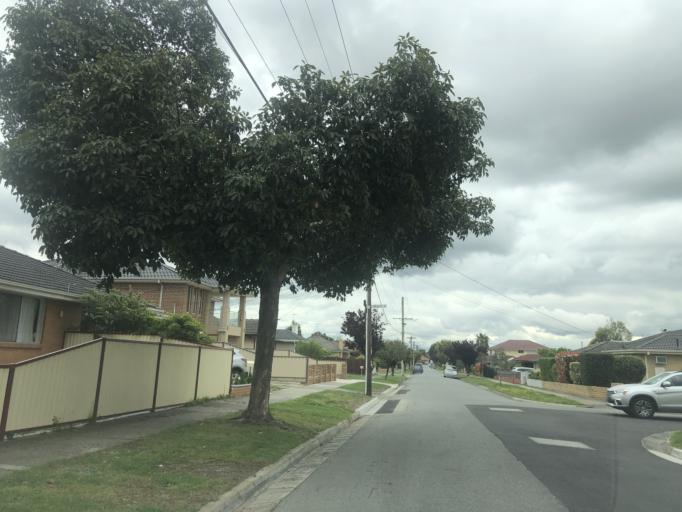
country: AU
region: Victoria
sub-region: Greater Dandenong
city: Dandenong North
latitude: -37.9732
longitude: 145.2135
